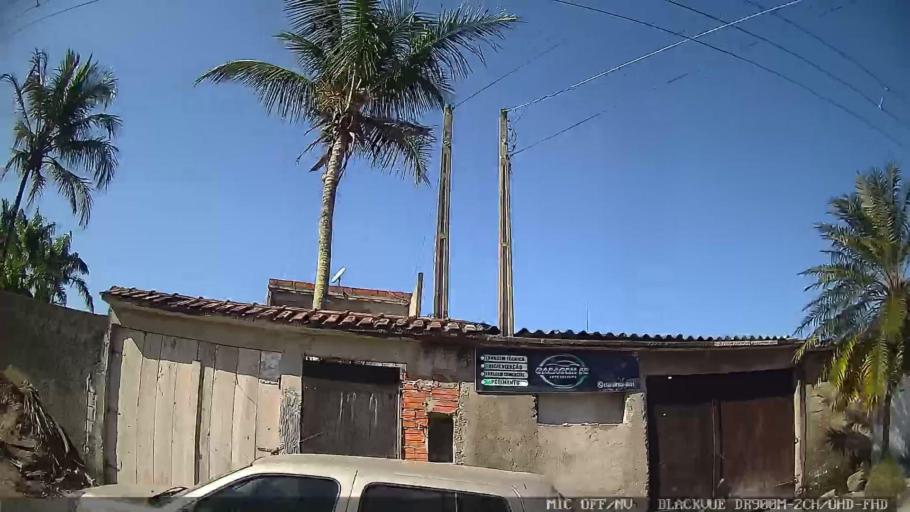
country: BR
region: Sao Paulo
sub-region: Guaruja
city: Guaruja
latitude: -23.9673
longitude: -46.2116
